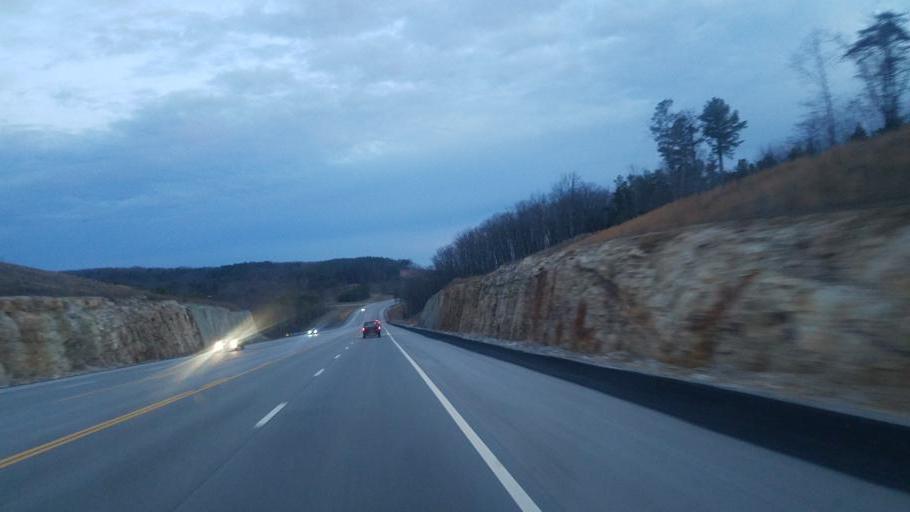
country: US
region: Tennessee
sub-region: Van Buren County
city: Spencer
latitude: 35.7629
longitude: -85.4611
